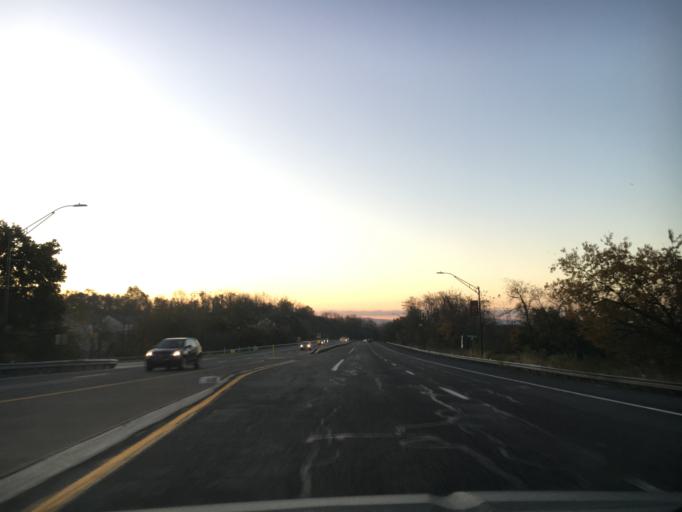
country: US
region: Pennsylvania
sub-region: Lehigh County
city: Egypt
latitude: 40.6816
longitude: -75.5196
